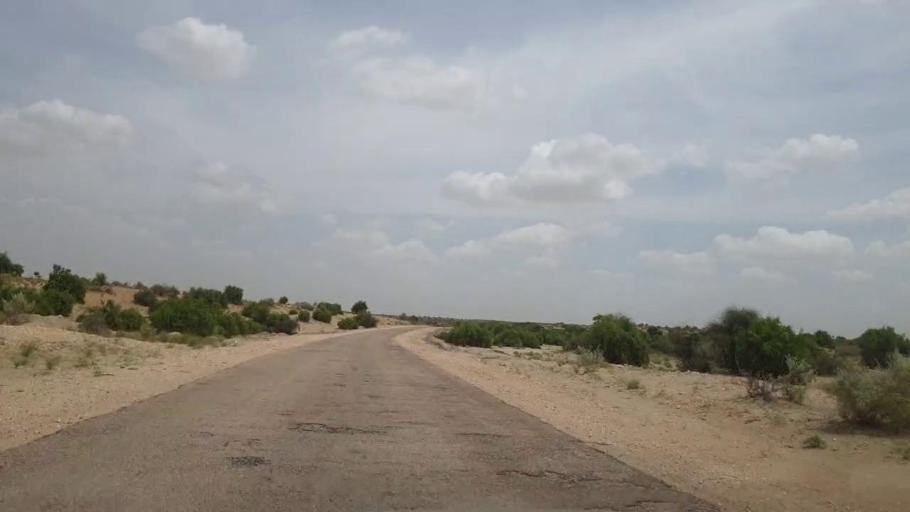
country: PK
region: Sindh
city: Kot Diji
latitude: 27.1878
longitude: 69.1698
